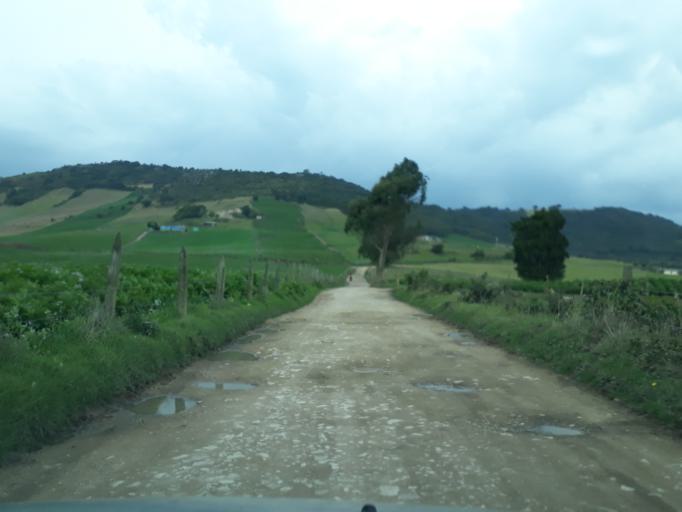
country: CO
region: Cundinamarca
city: Villapinzon
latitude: 5.2359
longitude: -73.6695
